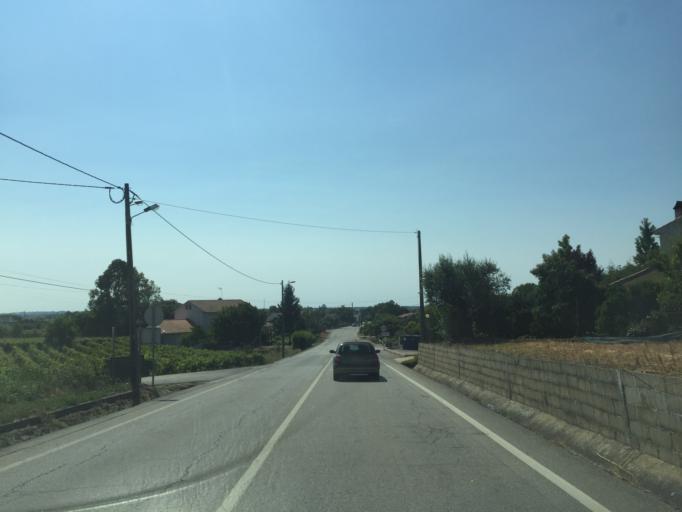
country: PT
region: Coimbra
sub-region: Cantanhede
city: Cantanhede
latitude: 40.3572
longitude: -8.5461
